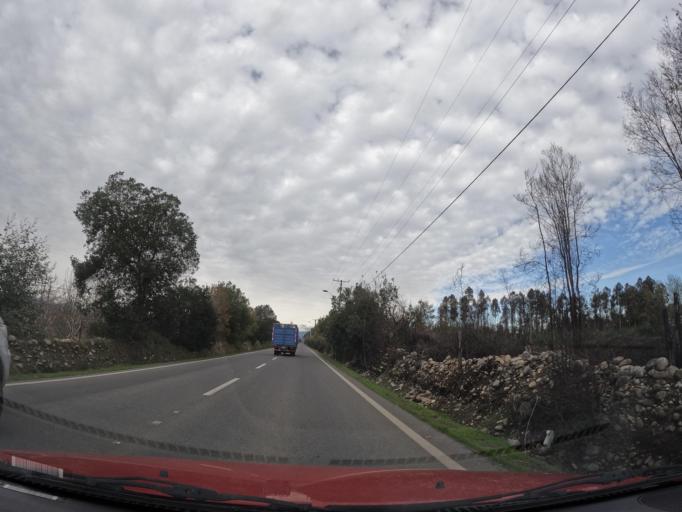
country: CL
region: Maule
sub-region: Provincia de Linares
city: Linares
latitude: -35.8887
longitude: -71.5290
